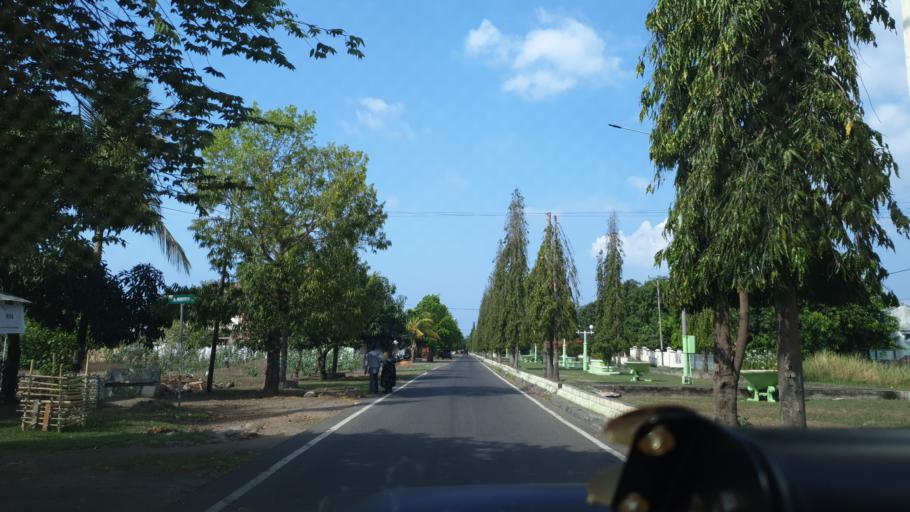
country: ID
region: East Nusa Tenggara
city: Waioti
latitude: -8.6338
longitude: 122.2358
